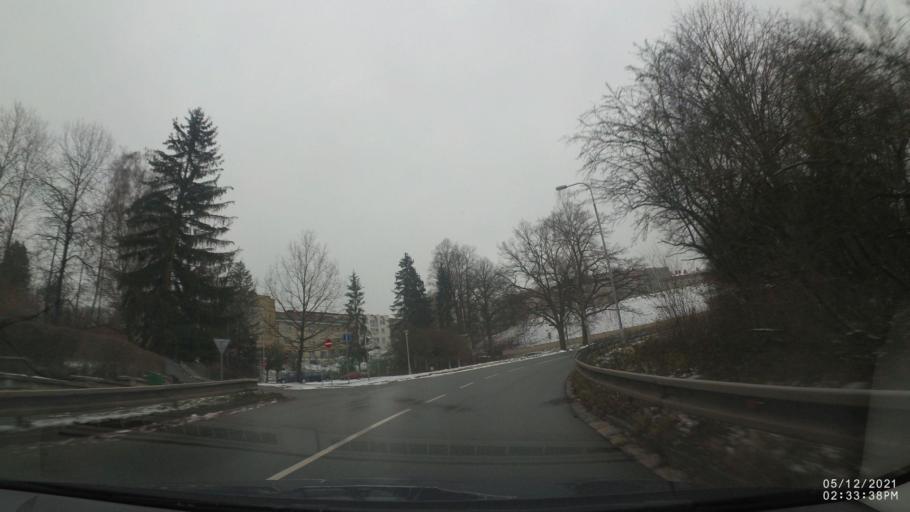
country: CZ
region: Kralovehradecky
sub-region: Okres Nachod
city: Nachod
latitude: 50.4083
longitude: 16.1649
